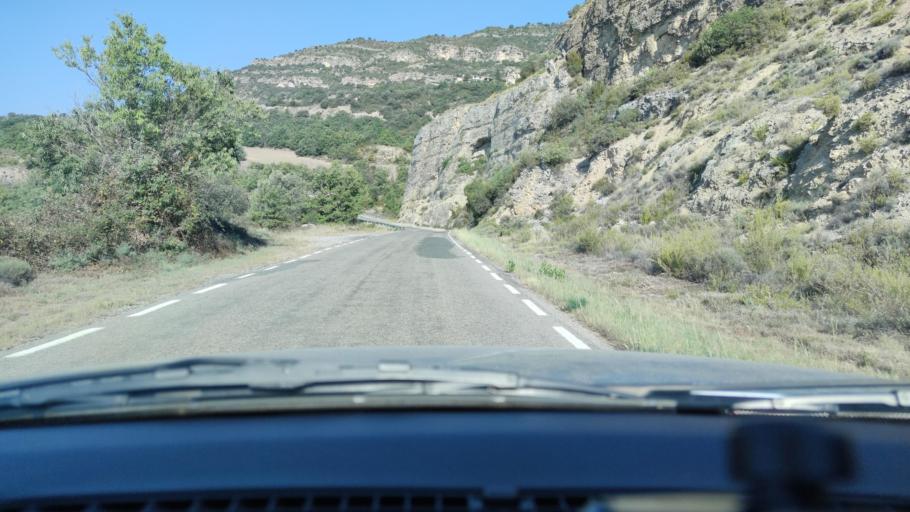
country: ES
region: Catalonia
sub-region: Provincia de Lleida
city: Llimiana
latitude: 42.0847
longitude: 0.8485
